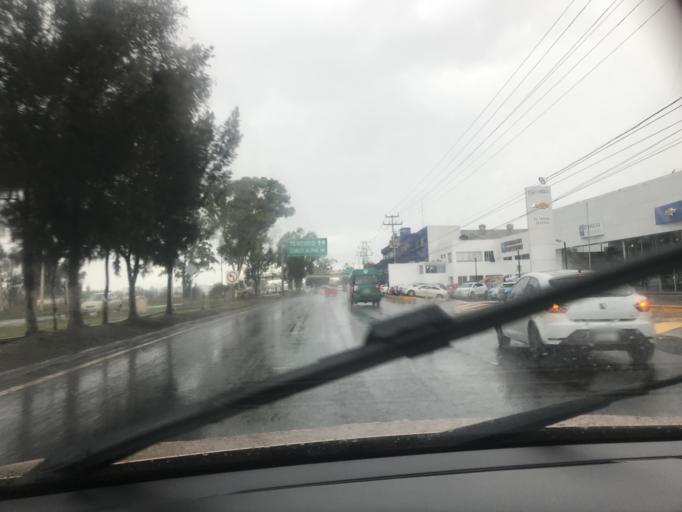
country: MX
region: Mexico
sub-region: Texcoco
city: Santa Martha
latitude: 19.4311
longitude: -98.9086
